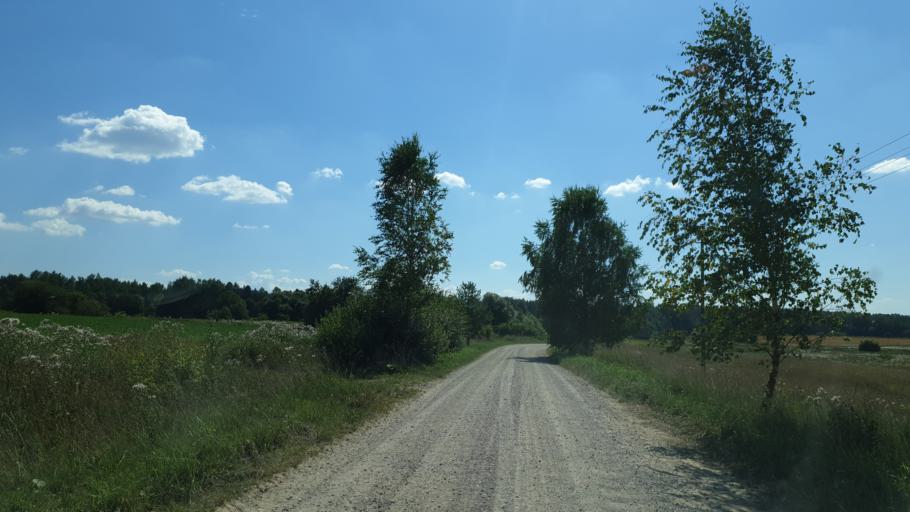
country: LT
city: Sirvintos
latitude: 54.9051
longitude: 24.9109
